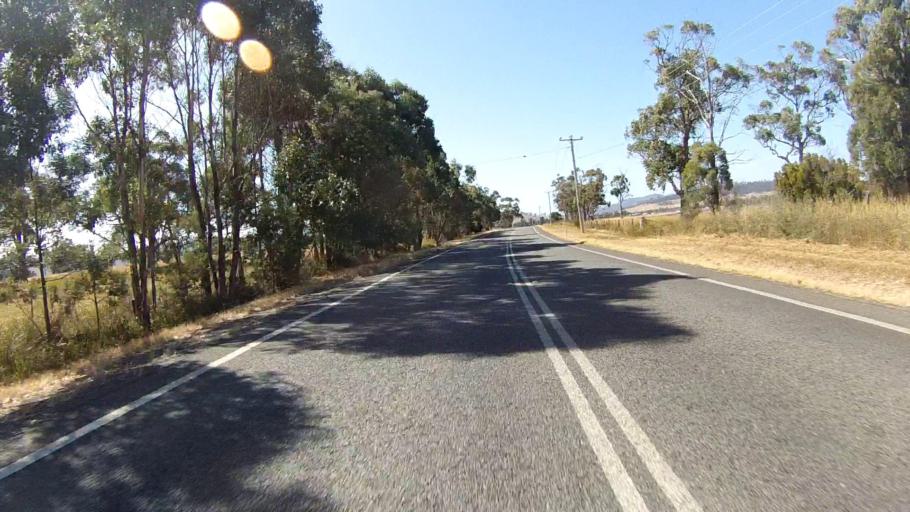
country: AU
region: Tasmania
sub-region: Sorell
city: Sorell
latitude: -42.5208
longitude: 147.8987
